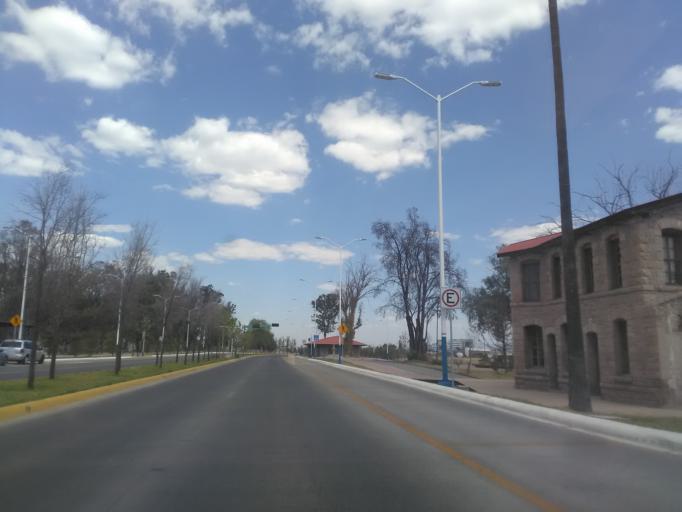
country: MX
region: Durango
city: Victoria de Durango
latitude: 24.0365
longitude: -104.6735
